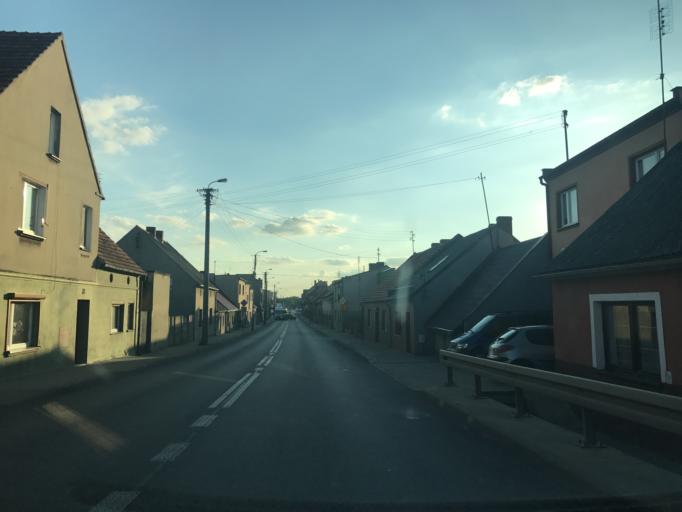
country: PL
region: Greater Poland Voivodeship
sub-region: Powiat gostynski
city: Piaski
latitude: 51.8848
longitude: 17.0744
